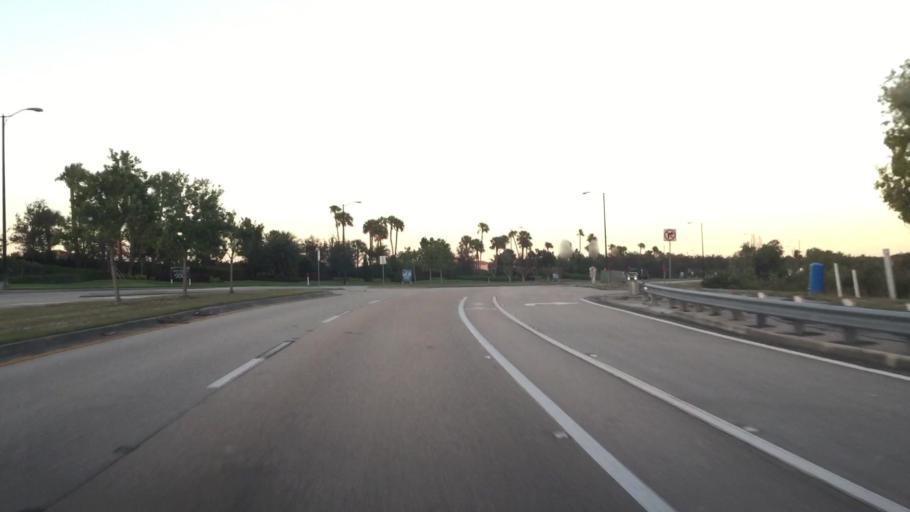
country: US
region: Florida
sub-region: Lee County
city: Gateway
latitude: 26.5660
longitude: -81.7860
